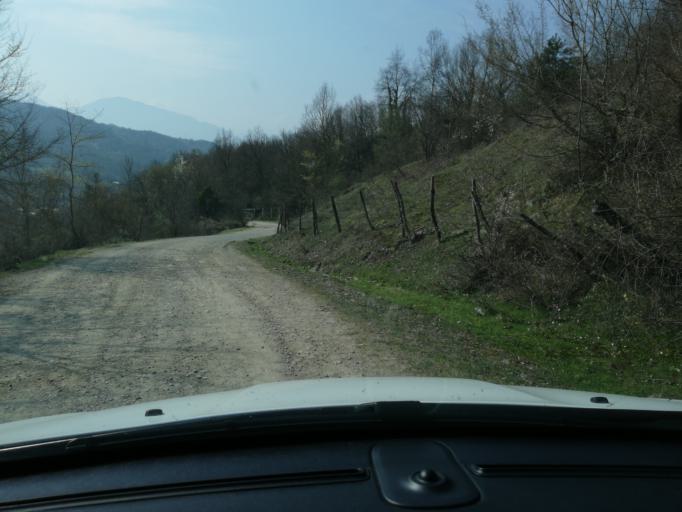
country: TR
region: Karabuk
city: Yenice
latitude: 41.2649
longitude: 32.3601
